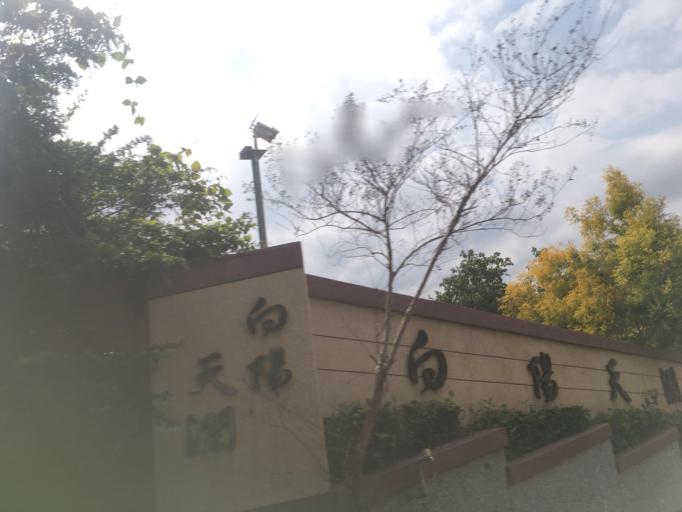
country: TW
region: Taiwan
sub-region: Miaoli
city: Miaoli
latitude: 24.4417
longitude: 120.7011
